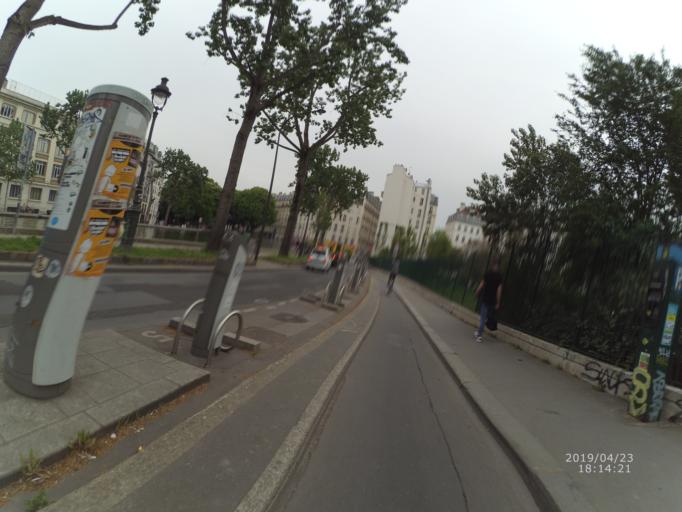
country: FR
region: Ile-de-France
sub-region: Paris
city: Paris
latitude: 48.8750
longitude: 2.3631
